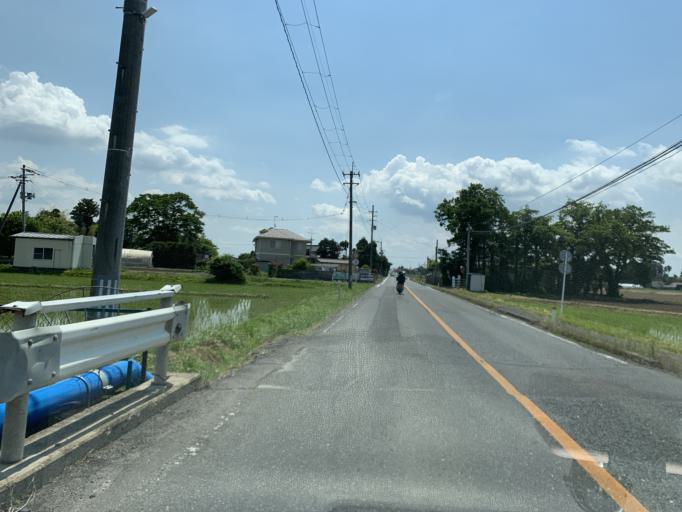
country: JP
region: Miyagi
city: Kogota
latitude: 38.5697
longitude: 141.0408
